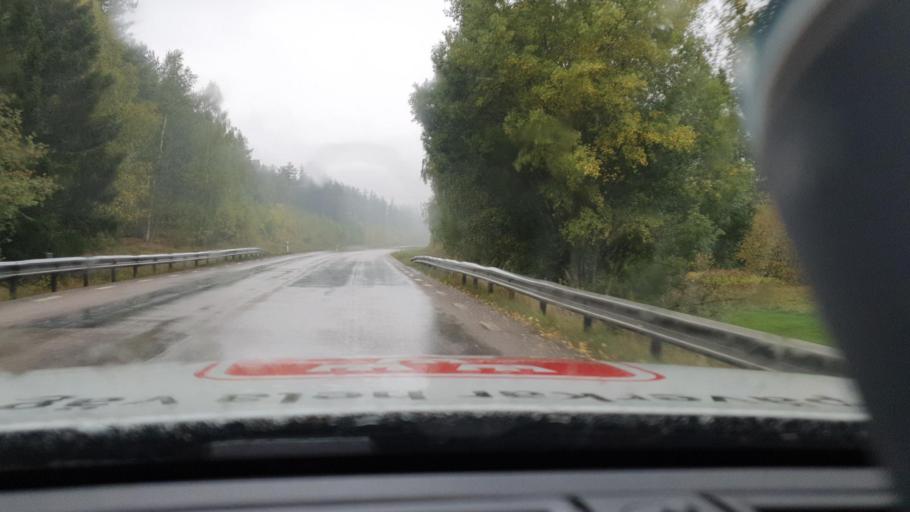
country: SE
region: Uppsala
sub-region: Tierps Kommun
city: Orbyhus
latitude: 60.2204
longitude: 17.6896
